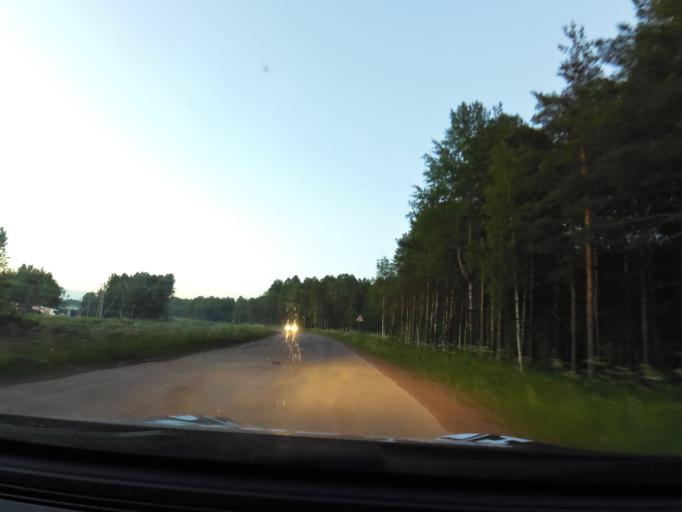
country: RU
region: Vologda
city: Vytegra
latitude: 60.9927
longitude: 36.3673
